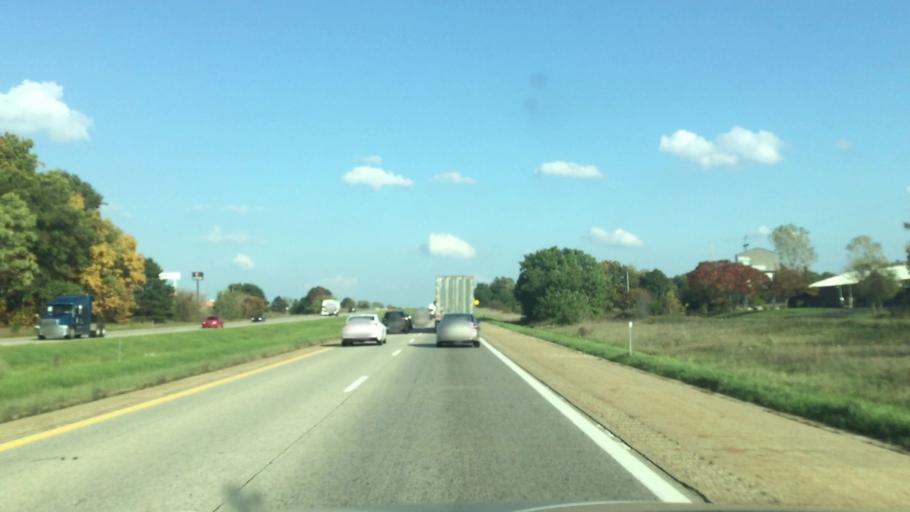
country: US
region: Michigan
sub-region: Jackson County
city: Concord
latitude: 42.2620
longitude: -84.6555
